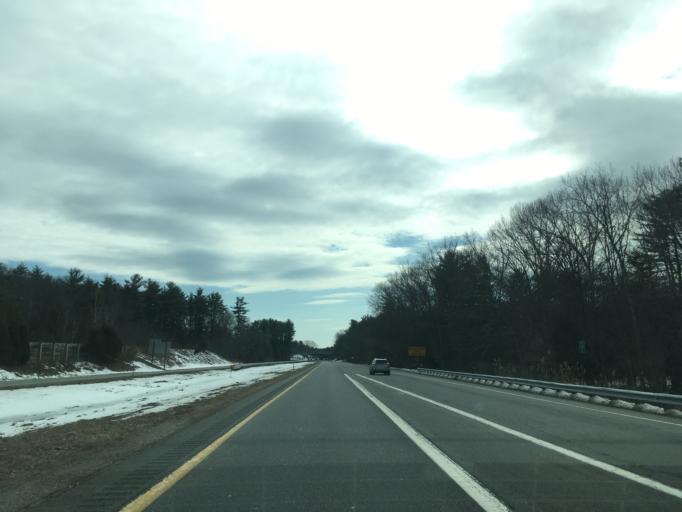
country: US
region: New Hampshire
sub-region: Rockingham County
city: Hampton
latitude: 42.9514
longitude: -70.8524
